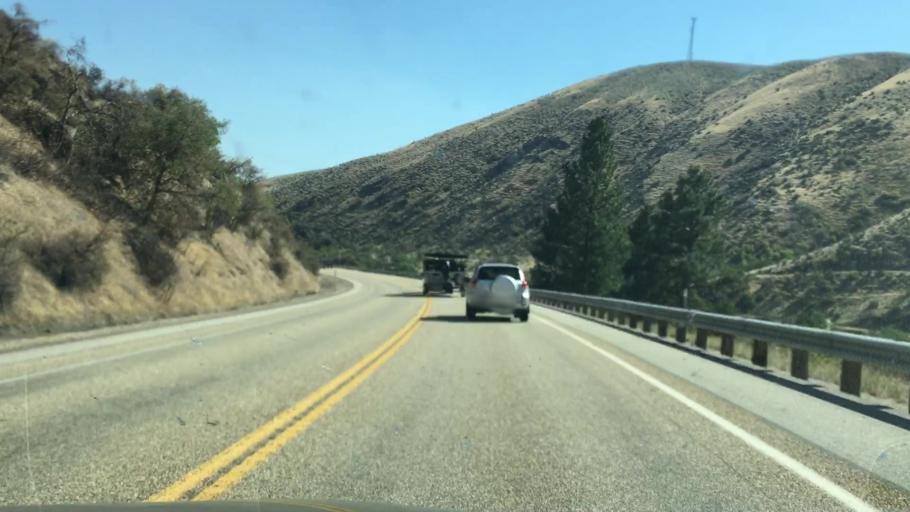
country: US
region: Idaho
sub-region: Ada County
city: Eagle
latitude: 43.9442
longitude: -116.1964
